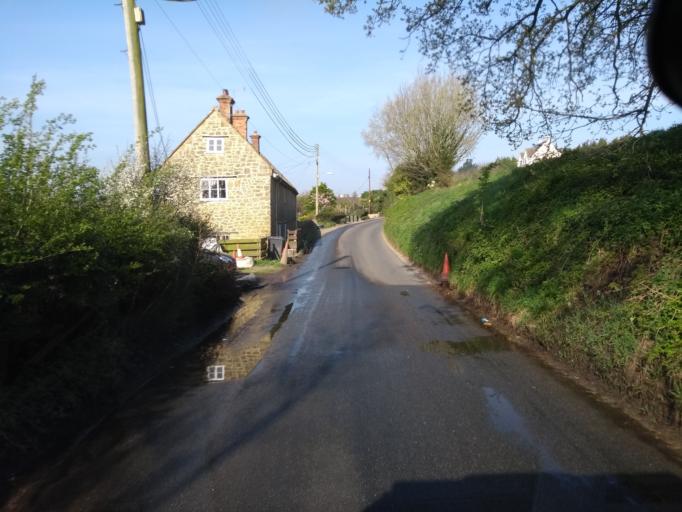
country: GB
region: England
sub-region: Somerset
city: Ilminster
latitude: 50.9260
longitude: -2.8983
